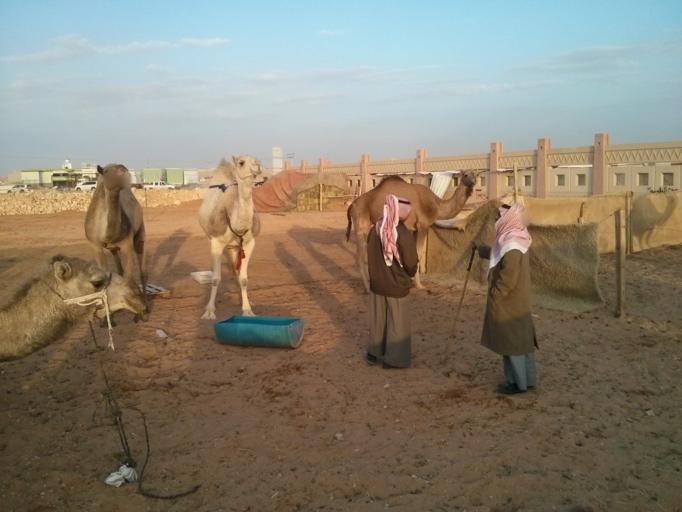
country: SA
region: Ar Riyad
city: Riyadh
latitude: 24.8563
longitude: 46.8491
